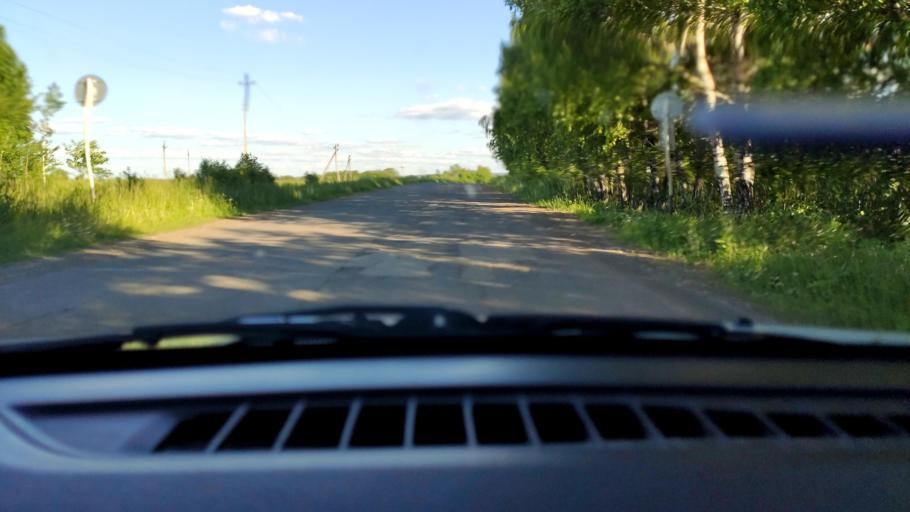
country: RU
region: Perm
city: Uinskoye
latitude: 57.0923
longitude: 56.5533
